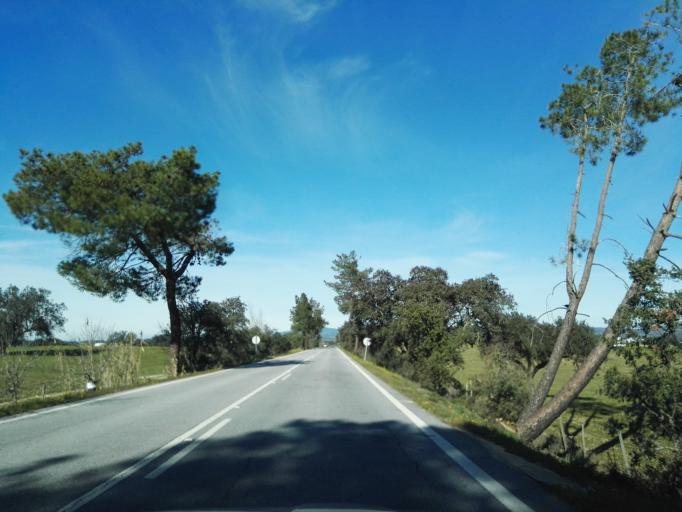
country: PT
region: Portalegre
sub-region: Arronches
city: Arronches
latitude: 39.0806
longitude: -7.2810
